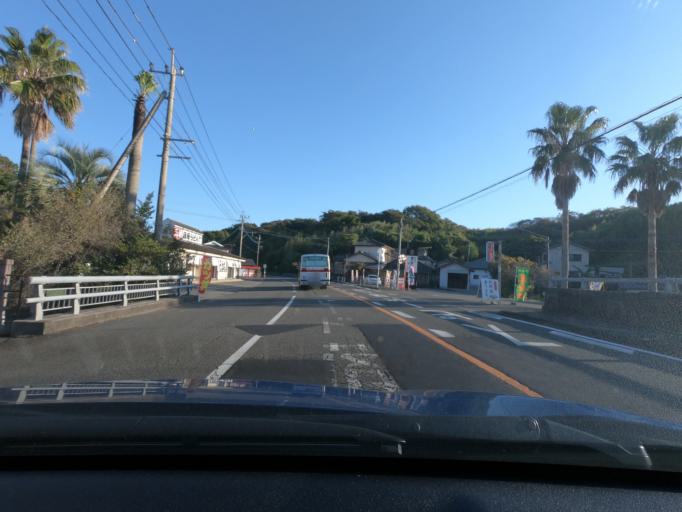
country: JP
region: Kagoshima
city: Akune
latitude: 31.9902
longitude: 130.1984
